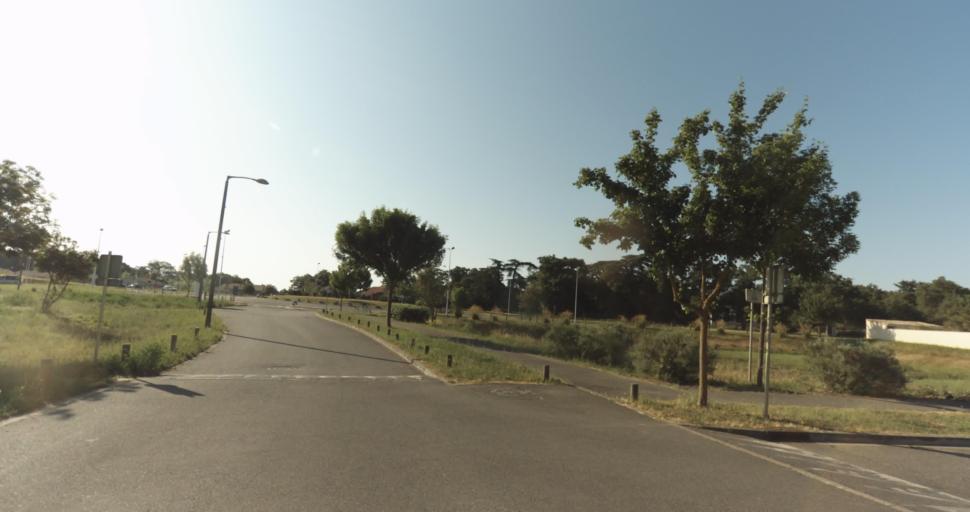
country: FR
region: Midi-Pyrenees
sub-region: Departement de la Haute-Garonne
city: La Salvetat-Saint-Gilles
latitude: 43.5706
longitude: 1.2445
